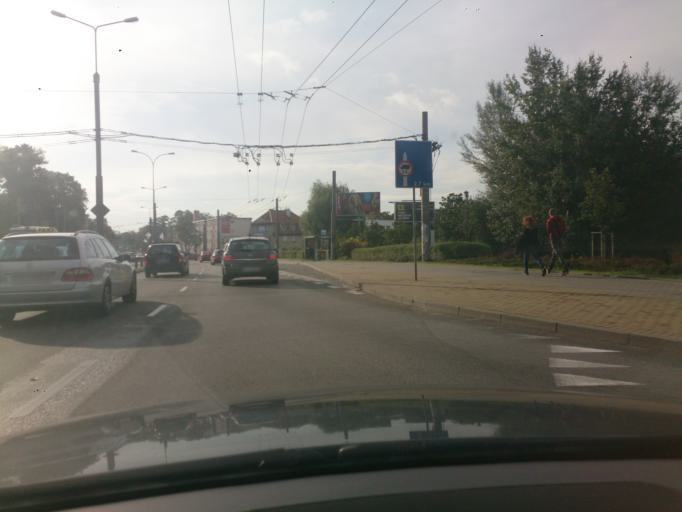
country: PL
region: Pomeranian Voivodeship
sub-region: Gdynia
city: Gdynia
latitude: 54.4849
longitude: 18.5459
